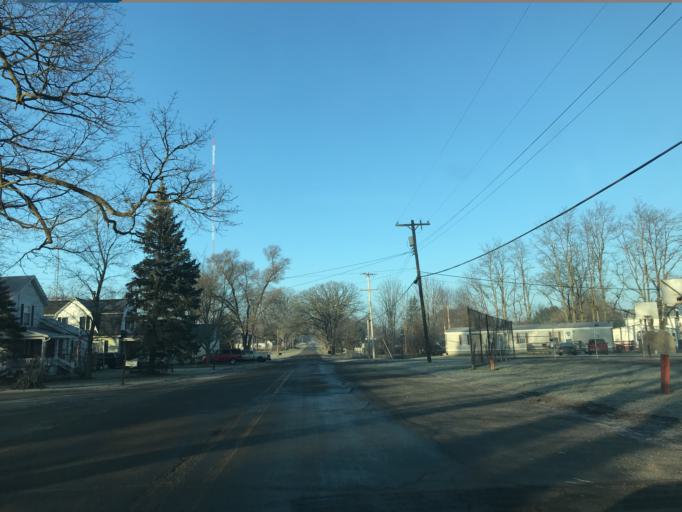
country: US
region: Michigan
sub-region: Eaton County
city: Eaton Rapids
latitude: 42.4439
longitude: -84.5629
